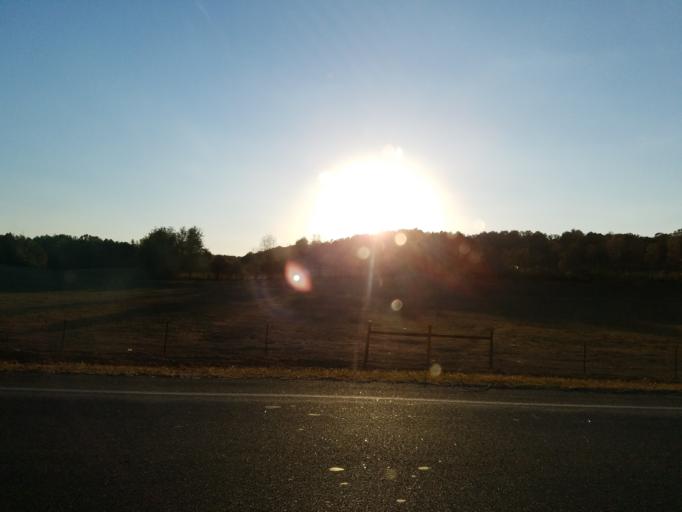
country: US
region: Georgia
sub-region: Gordon County
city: Calhoun
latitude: 34.5256
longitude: -84.9713
